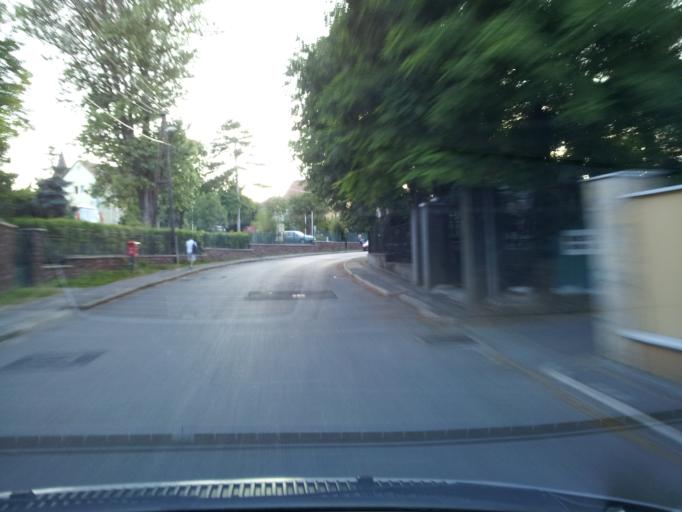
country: HU
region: Veszprem
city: Balatonalmadi
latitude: 47.0303
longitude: 18.0211
